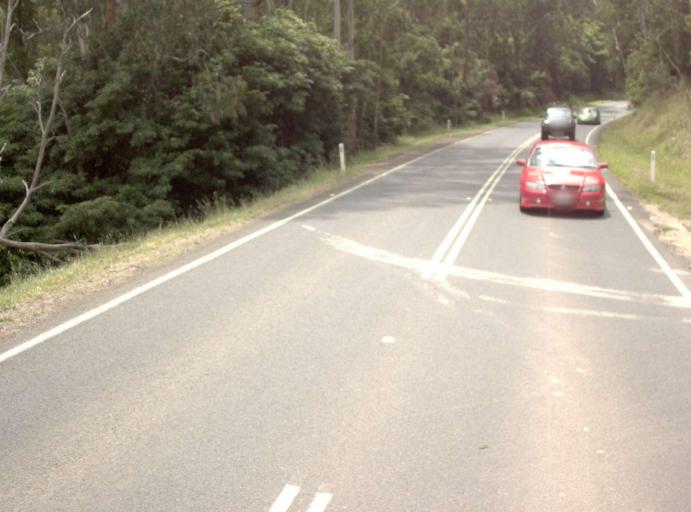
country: AU
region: Victoria
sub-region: Latrobe
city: Traralgon
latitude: -38.4340
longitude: 146.7337
